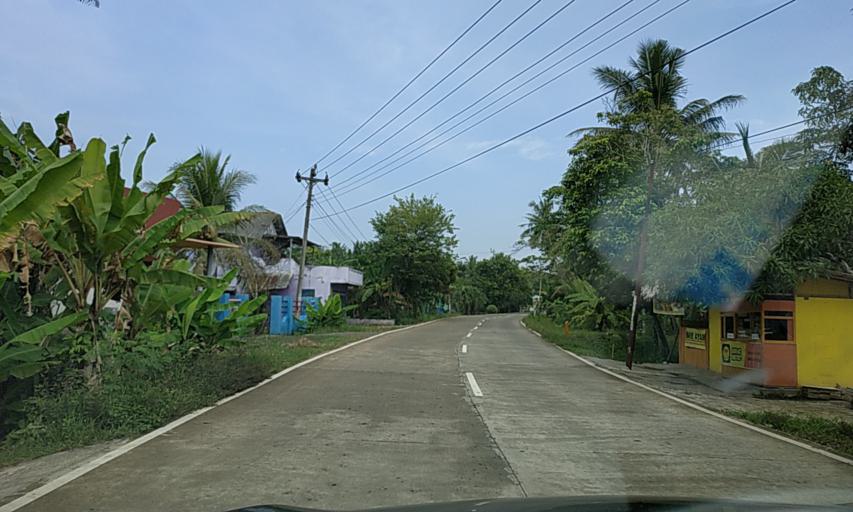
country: ID
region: Central Java
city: Tambangan
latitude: -7.4829
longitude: 108.8359
